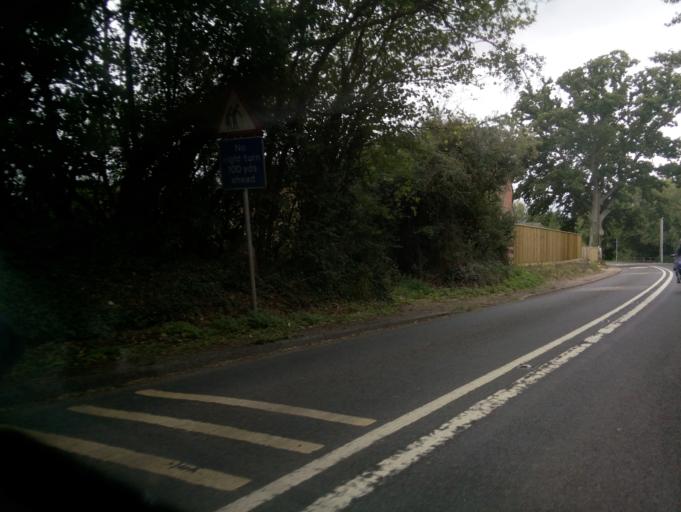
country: GB
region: England
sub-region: Devon
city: Cullompton
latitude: 50.8466
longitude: -3.3931
